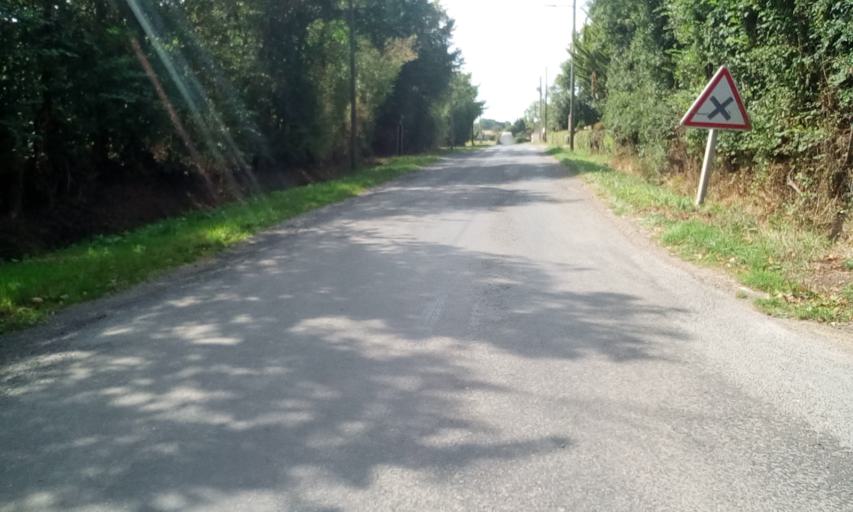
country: FR
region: Lower Normandy
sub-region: Departement du Calvados
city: Argences
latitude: 49.1541
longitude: -0.1475
